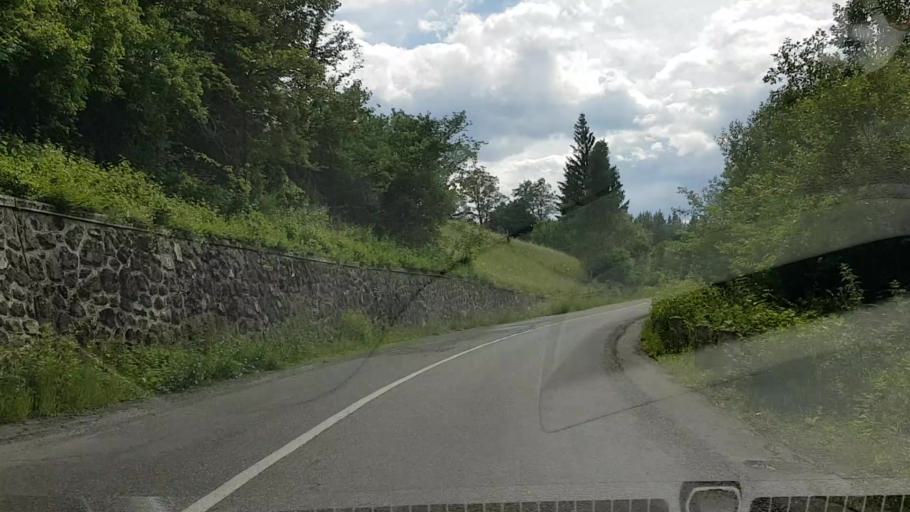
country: RO
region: Neamt
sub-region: Comuna Ceahlau
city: Ceahlau
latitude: 47.0736
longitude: 25.9636
